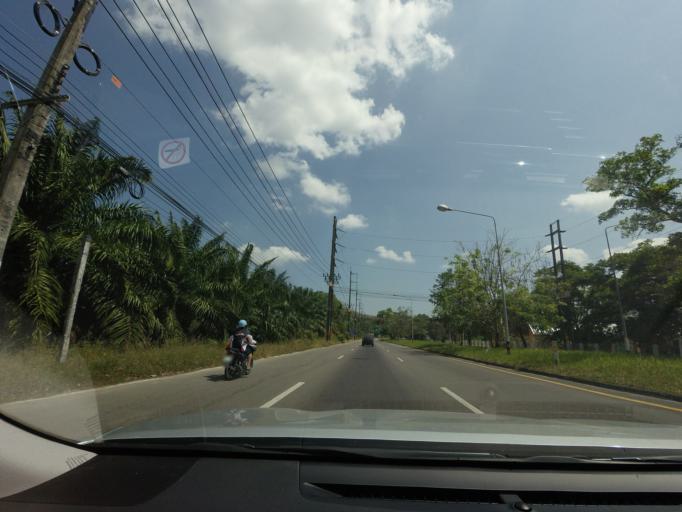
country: TH
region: Phangnga
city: Thai Mueang
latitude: 8.2715
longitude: 98.3334
